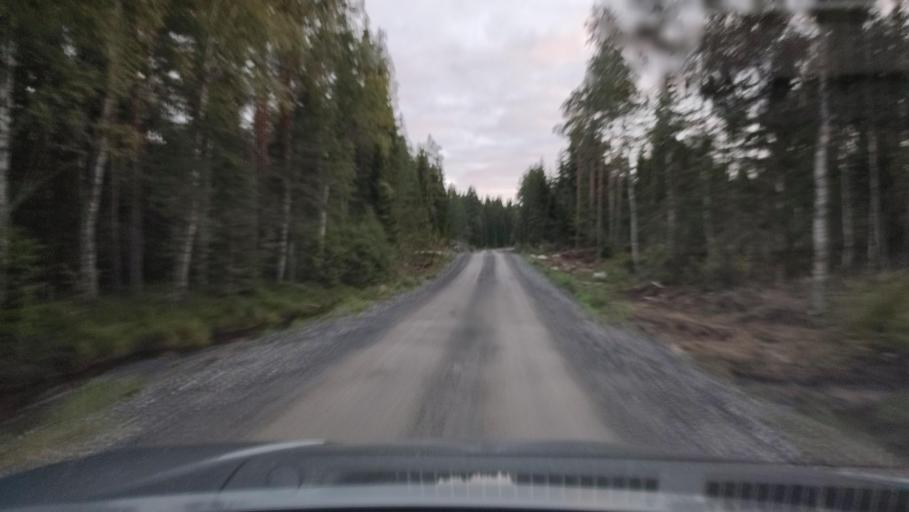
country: FI
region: Ostrobothnia
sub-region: Sydosterbotten
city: Kristinestad
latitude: 62.1912
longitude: 21.5417
